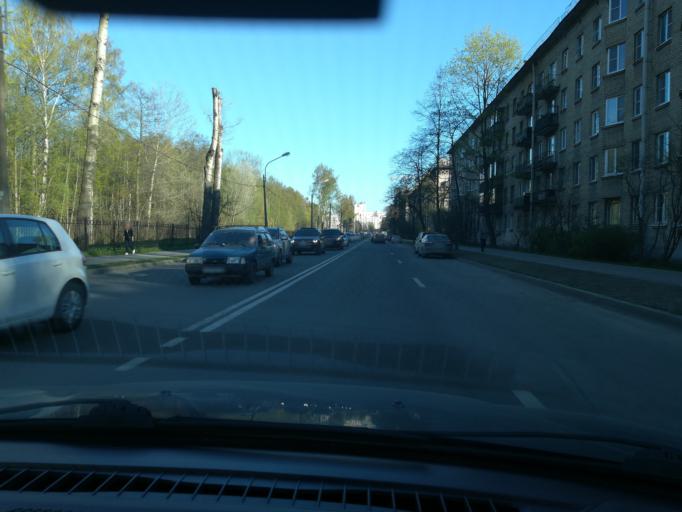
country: RU
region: St.-Petersburg
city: Vasyl'evsky Ostrov
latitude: 59.9430
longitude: 30.2395
